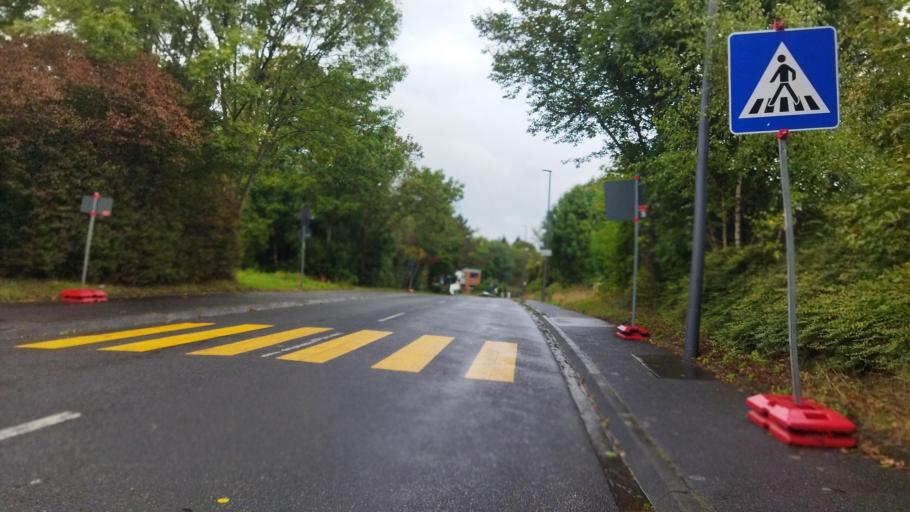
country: DE
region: North Rhine-Westphalia
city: Wesseling
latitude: 50.8526
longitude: 6.9675
